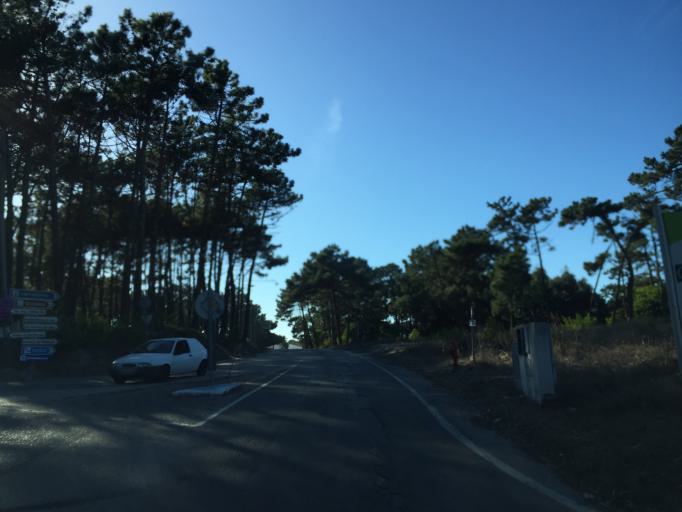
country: PT
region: Coimbra
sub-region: Figueira da Foz
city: Buarcos
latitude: 40.2151
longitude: -8.8838
